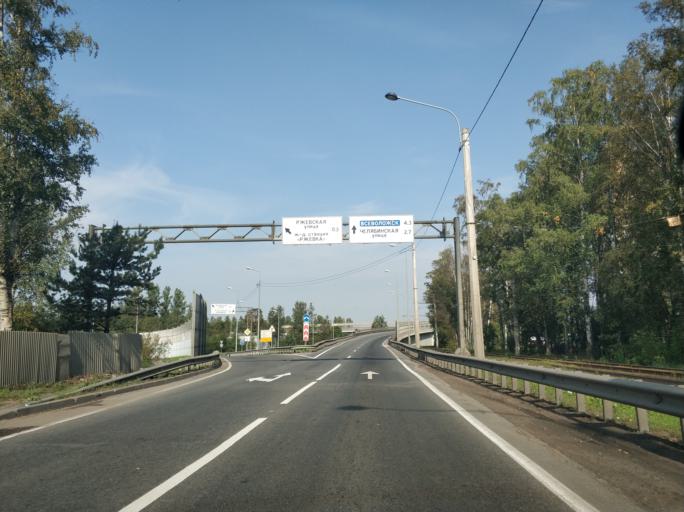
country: RU
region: St.-Petersburg
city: Krasnogvargeisky
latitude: 59.9781
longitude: 30.5059
